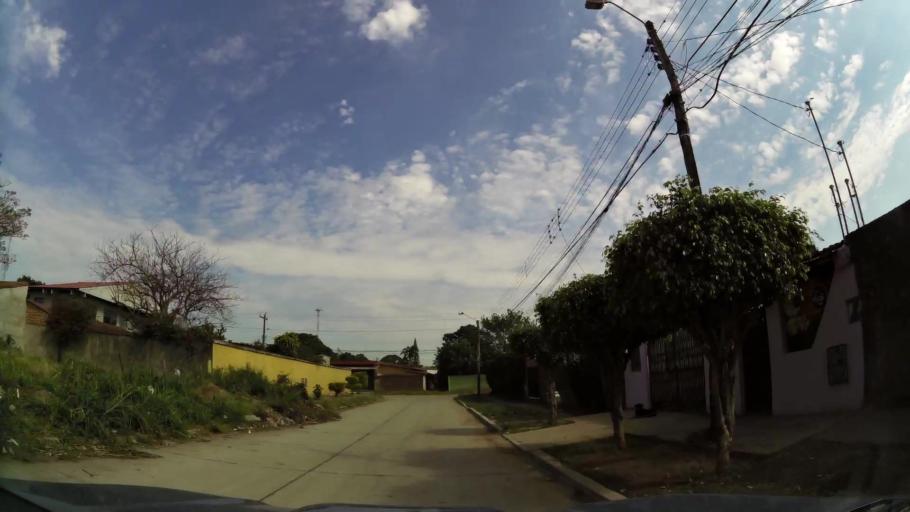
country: BO
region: Santa Cruz
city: Santa Cruz de la Sierra
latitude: -17.7272
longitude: -63.1548
